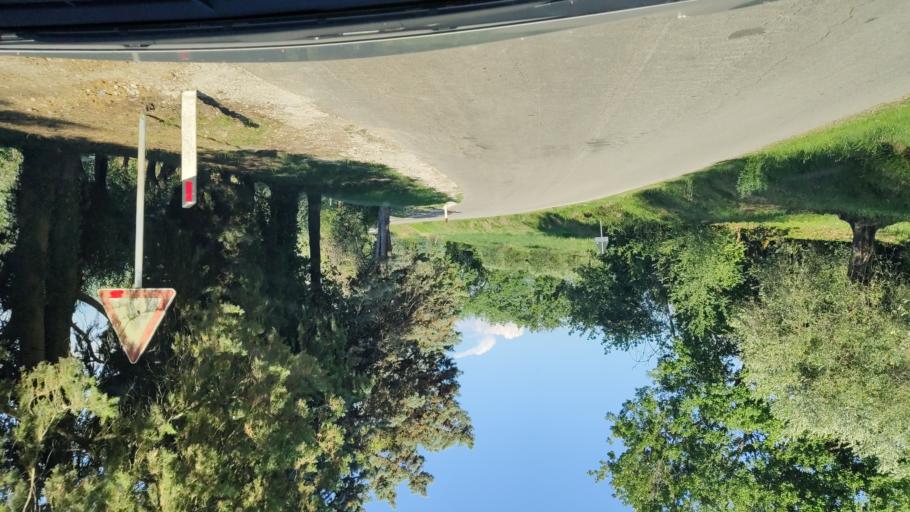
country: IT
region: Umbria
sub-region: Provincia di Terni
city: Penna in Teverina
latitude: 42.4881
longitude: 12.3608
